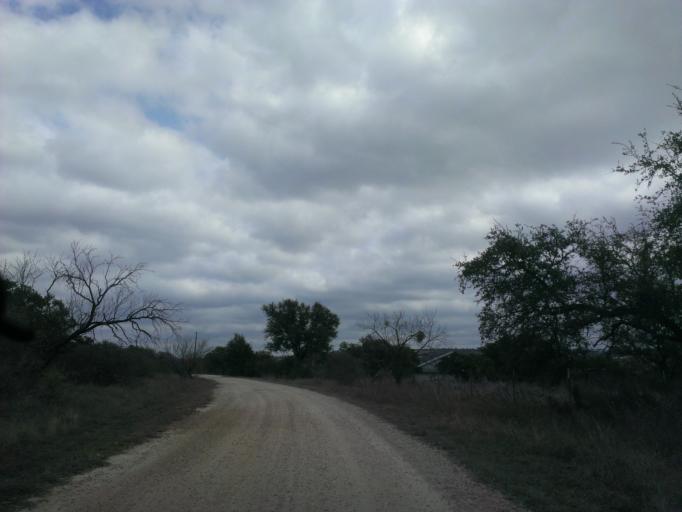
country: US
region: Texas
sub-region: Travis County
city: Briarcliff
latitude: 30.3869
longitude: -98.0921
